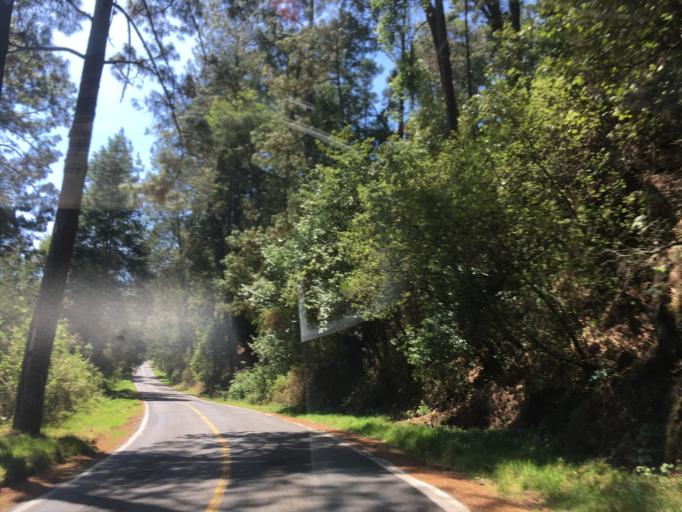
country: MX
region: Michoacan
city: Tzitzio
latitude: 19.6479
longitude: -100.7893
